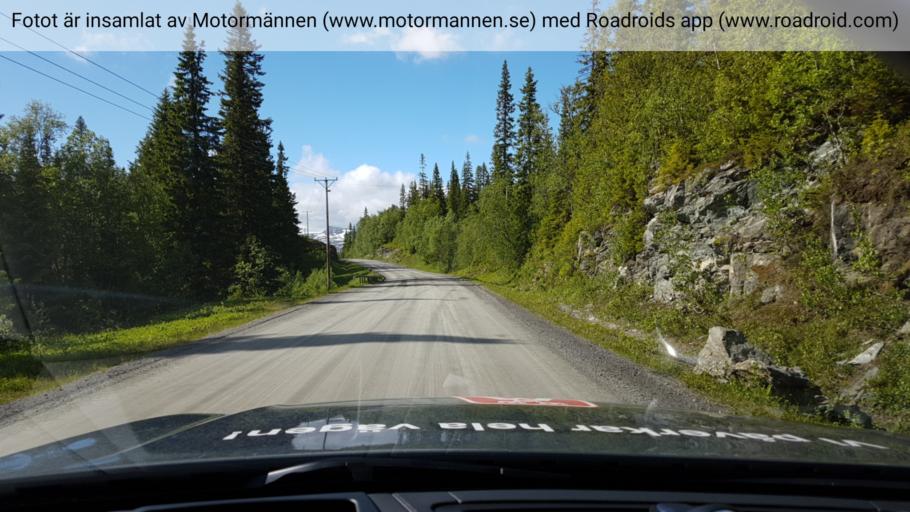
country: SE
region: Jaemtland
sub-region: Are Kommun
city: Are
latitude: 63.6766
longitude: 12.8179
